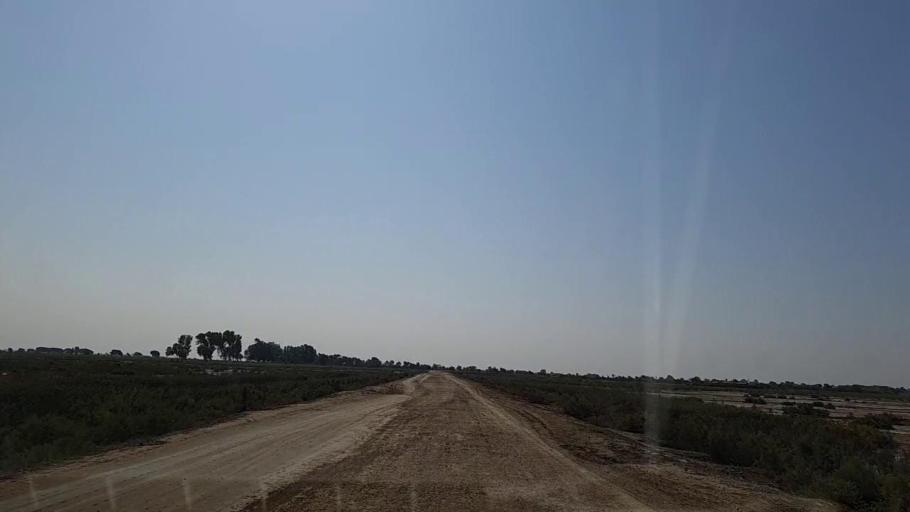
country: PK
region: Sindh
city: Chuhar Jamali
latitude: 24.5023
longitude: 68.0984
